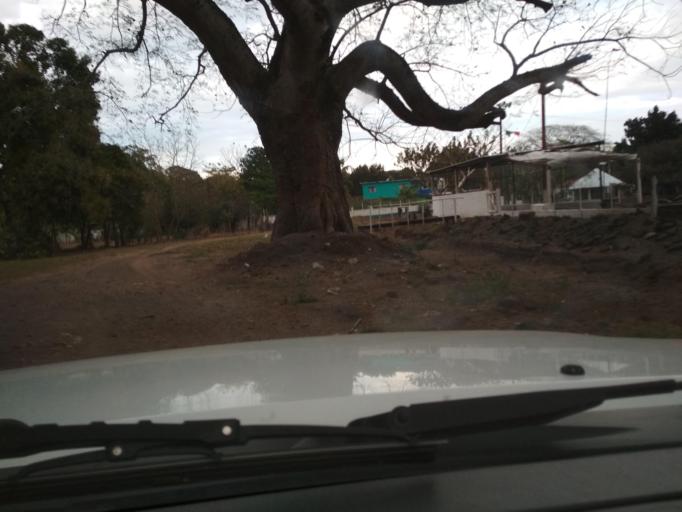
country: MX
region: Veracruz
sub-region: Veracruz
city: Delfino Victoria (Santa Fe)
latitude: 19.1672
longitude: -96.2618
